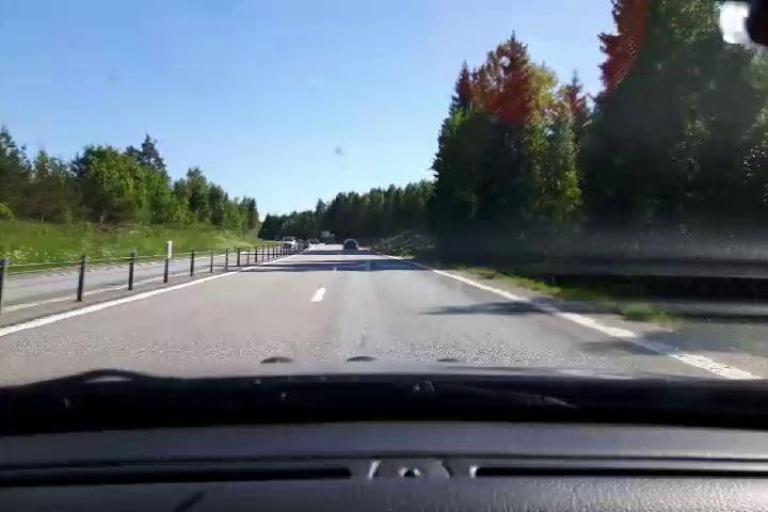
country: SE
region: Gaevleborg
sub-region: Gavle Kommun
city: Norrsundet
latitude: 60.9275
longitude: 17.0097
